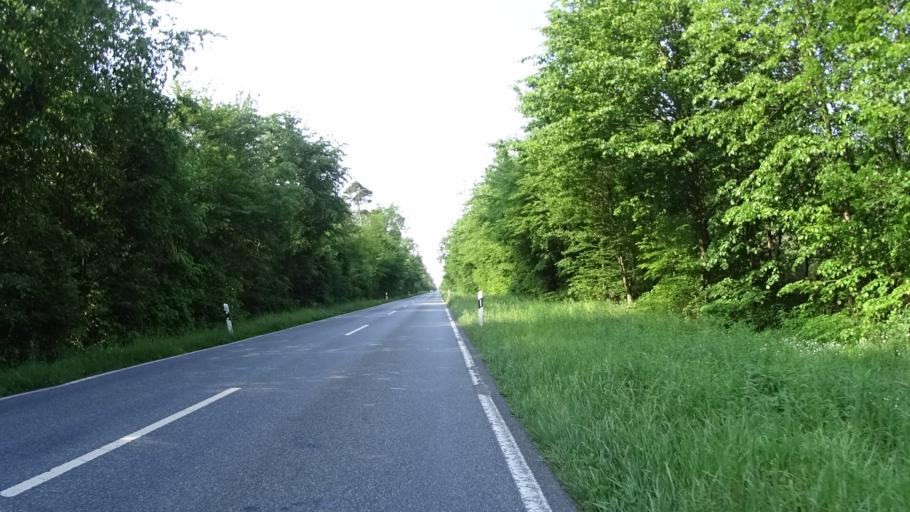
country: DE
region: Baden-Wuerttemberg
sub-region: Karlsruhe Region
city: Reilingen
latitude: 49.2777
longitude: 8.5620
